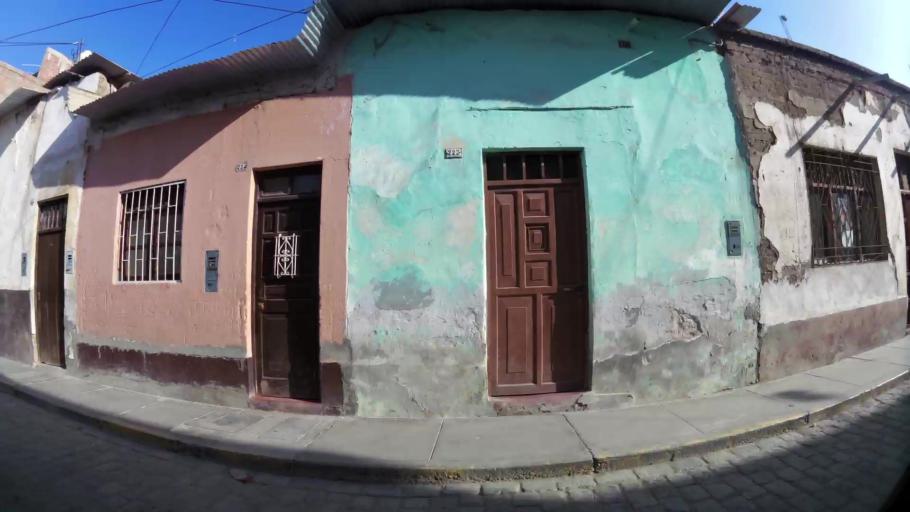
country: PE
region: Lambayeque
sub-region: Provincia de Chiclayo
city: Chiclayo
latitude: -6.7742
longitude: -79.8421
